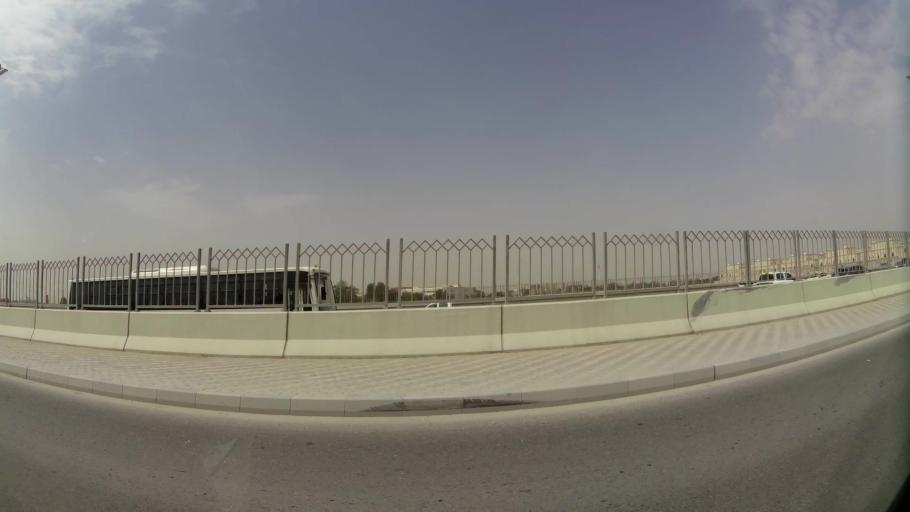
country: QA
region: Baladiyat ar Rayyan
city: Ar Rayyan
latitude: 25.2998
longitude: 51.4745
